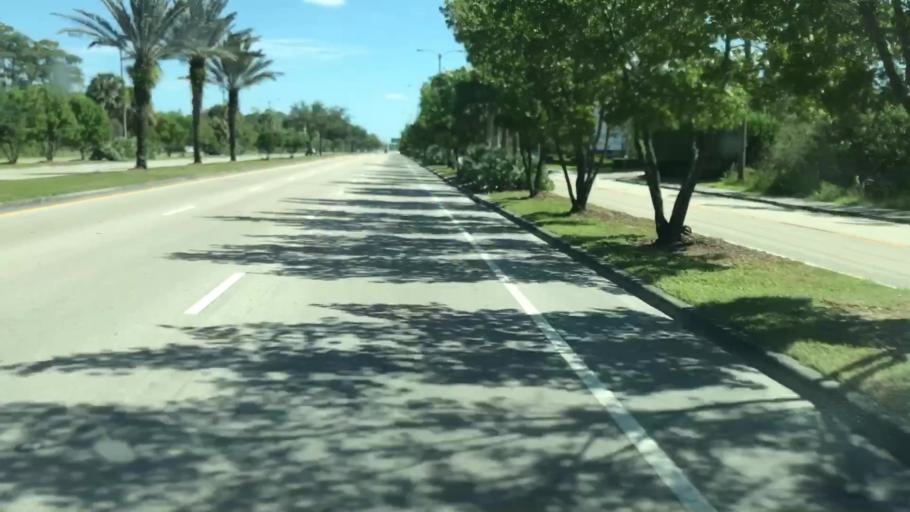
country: US
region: Florida
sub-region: Lee County
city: Gateway
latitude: 26.5475
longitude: -81.7826
